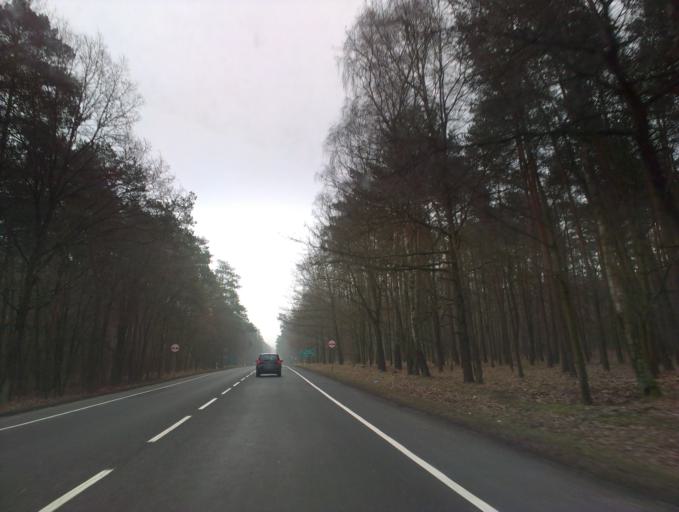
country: PL
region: Greater Poland Voivodeship
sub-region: Powiat pilski
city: Ujscie
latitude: 53.0210
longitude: 16.8198
